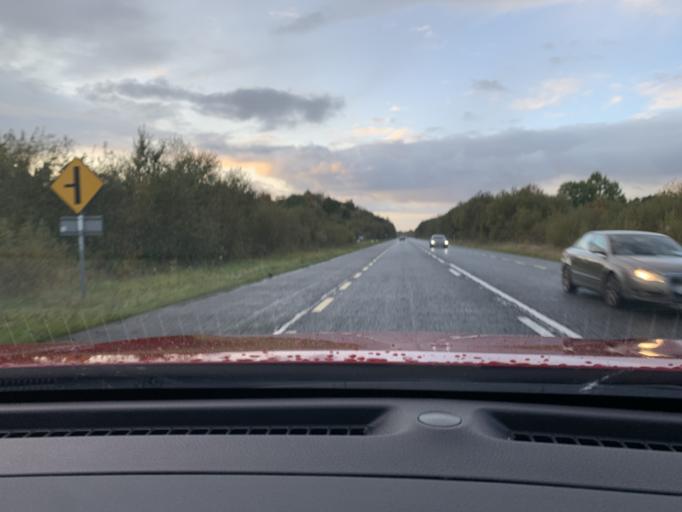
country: IE
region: Connaught
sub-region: County Leitrim
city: Carrick-on-Shannon
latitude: 53.9511
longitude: -8.1508
